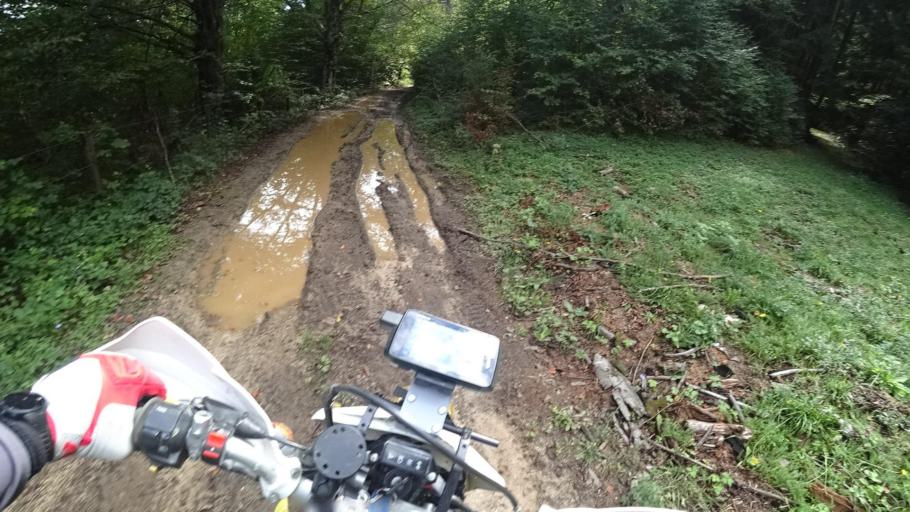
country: BA
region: Republika Srpska
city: Mrkonjic Grad
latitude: 44.5440
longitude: 17.1033
